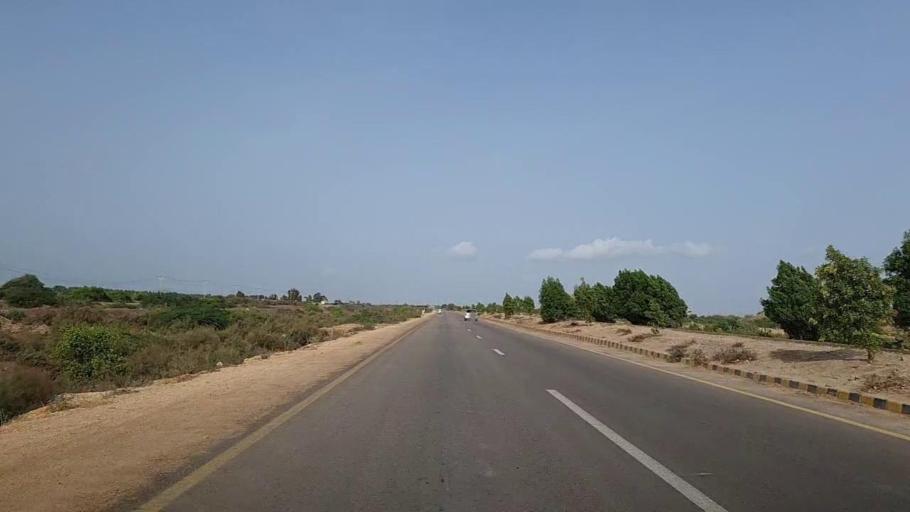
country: PK
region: Sindh
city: Thatta
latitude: 24.7421
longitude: 67.8082
